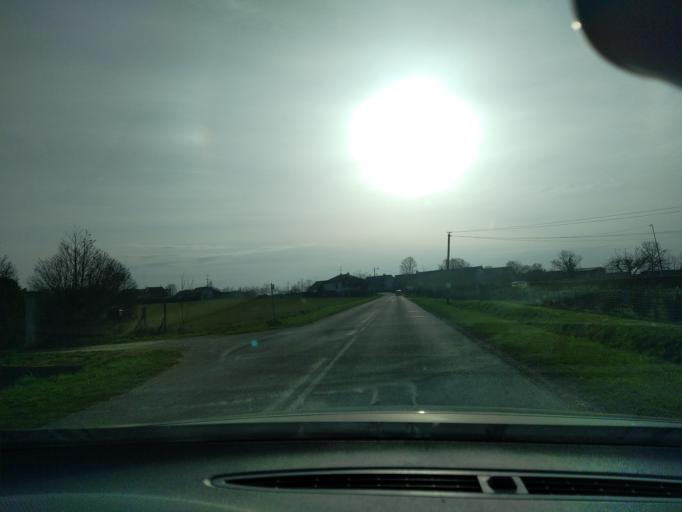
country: FR
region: Franche-Comte
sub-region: Departement du Jura
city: Chaussin
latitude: 46.9825
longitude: 5.4444
